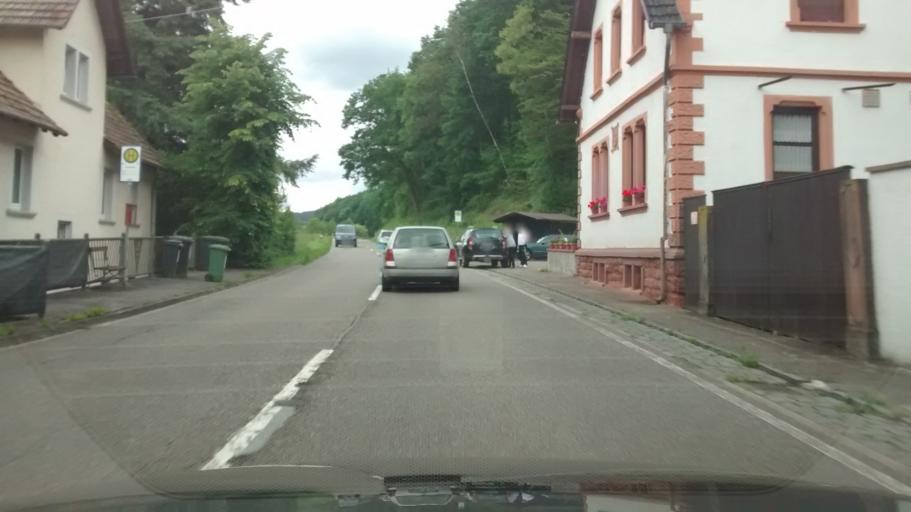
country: DE
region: Rheinland-Pfalz
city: Dorrenbach
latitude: 49.1104
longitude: 7.9599
